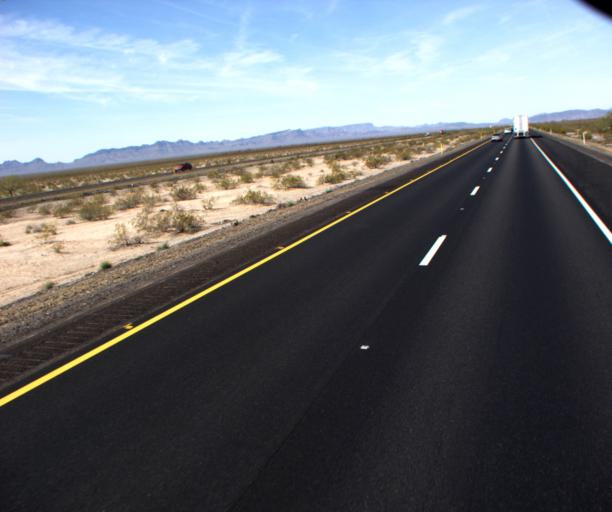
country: US
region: Arizona
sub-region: La Paz County
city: Salome
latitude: 33.6213
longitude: -113.7001
